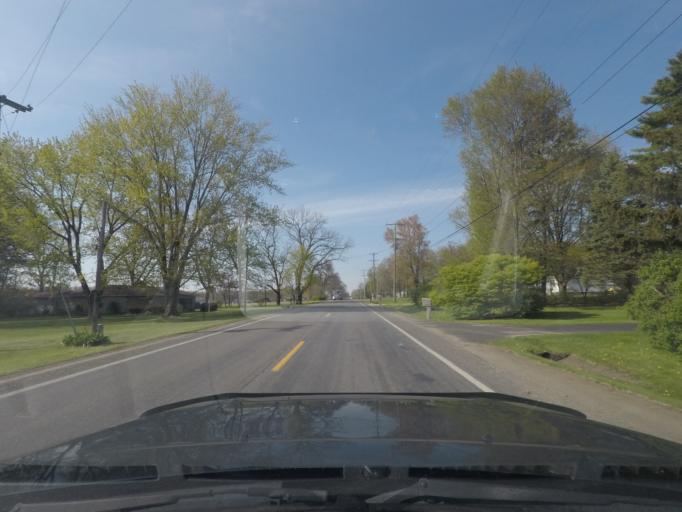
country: US
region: Michigan
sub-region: Berrien County
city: Niles
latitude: 41.7901
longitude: -86.2547
